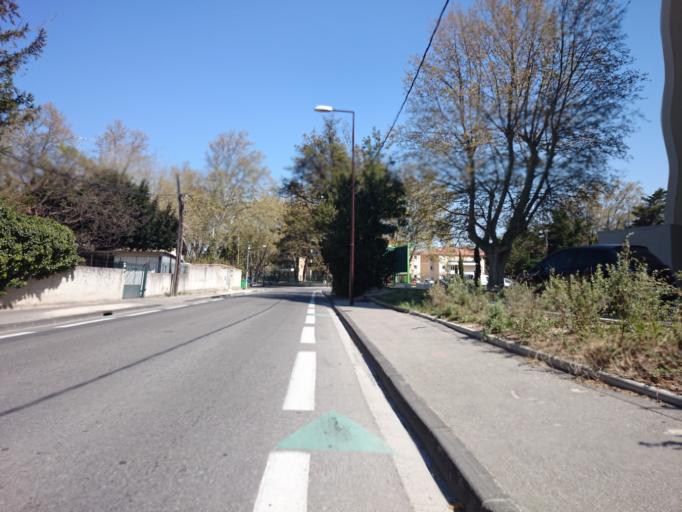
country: FR
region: Provence-Alpes-Cote d'Azur
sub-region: Departement du Vaucluse
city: Avignon
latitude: 43.9362
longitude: 4.7959
